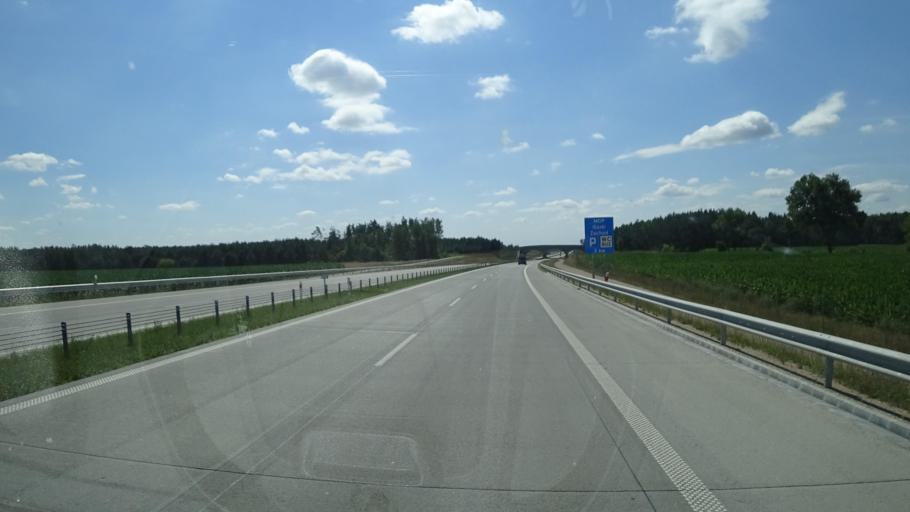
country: PL
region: Podlasie
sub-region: Powiat kolnenski
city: Stawiski
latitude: 53.2901
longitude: 22.1454
